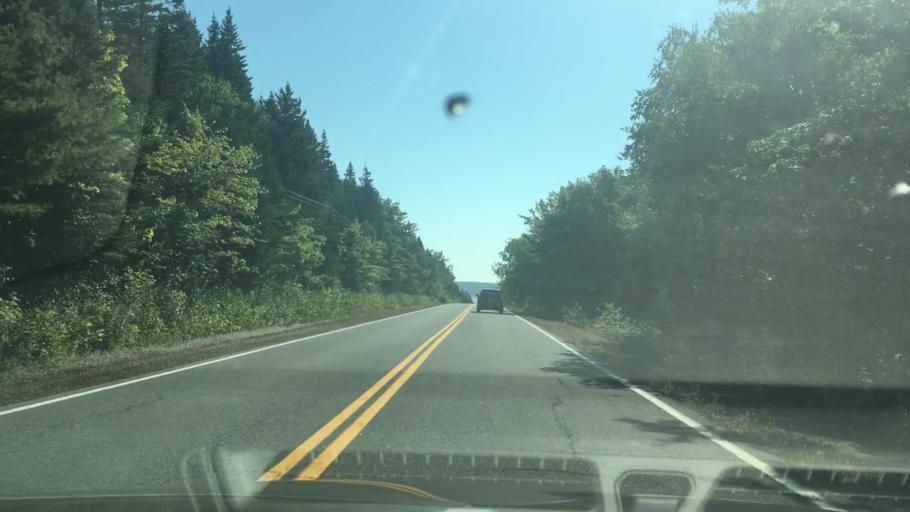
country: CA
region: Nova Scotia
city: Cole Harbour
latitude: 44.8160
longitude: -62.8793
